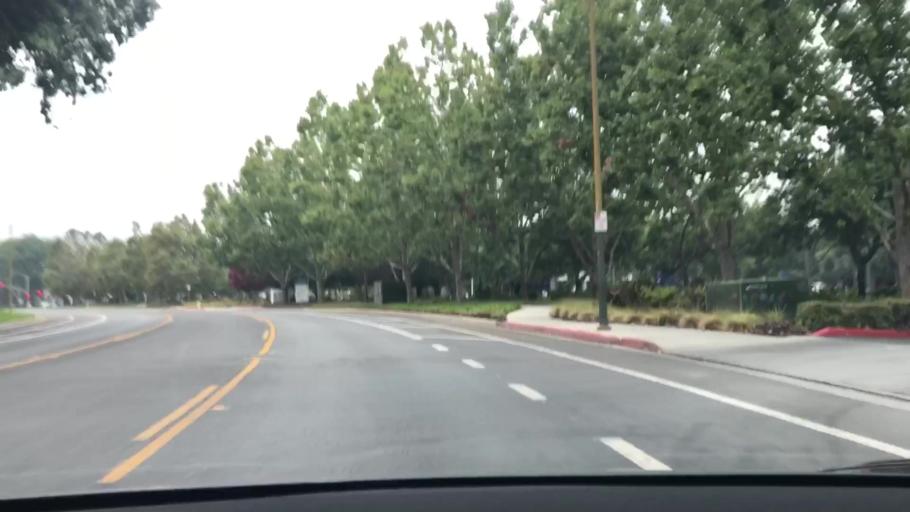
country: US
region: California
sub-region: Santa Clara County
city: Seven Trees
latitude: 37.2373
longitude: -121.7825
